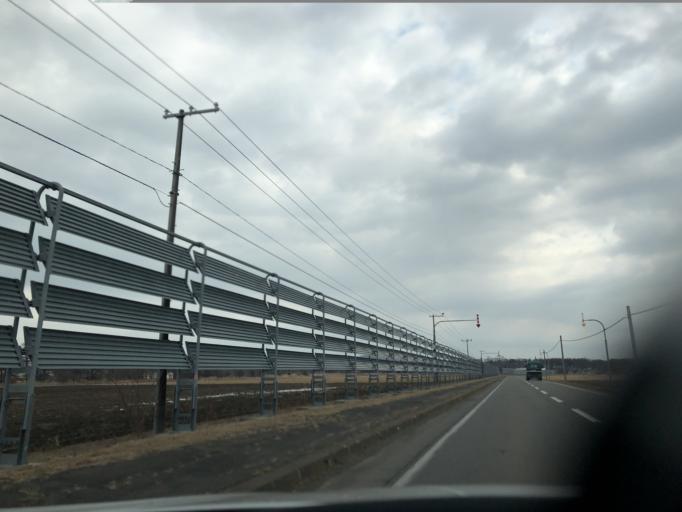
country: JP
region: Hokkaido
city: Chitose
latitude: 42.7616
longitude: 141.7645
